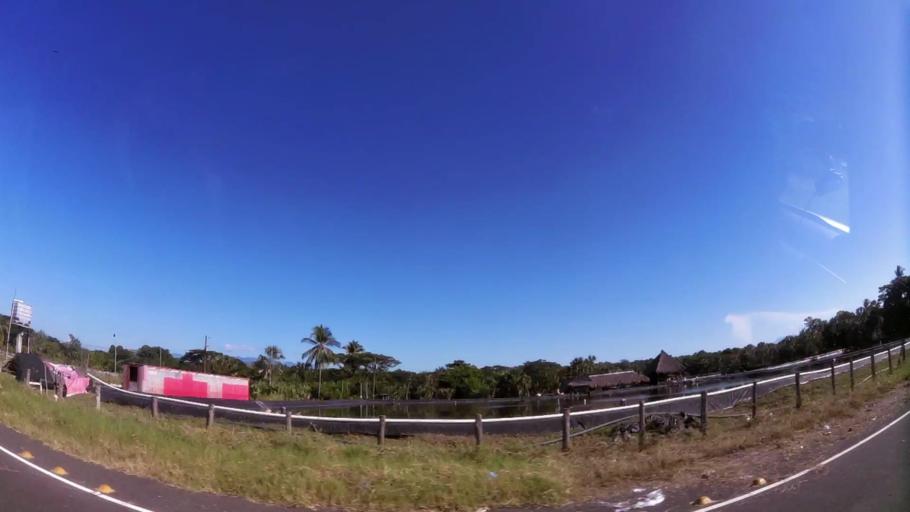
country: GT
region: Santa Rosa
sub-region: Municipio de Taxisco
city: Taxisco
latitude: 13.8740
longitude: -90.4253
